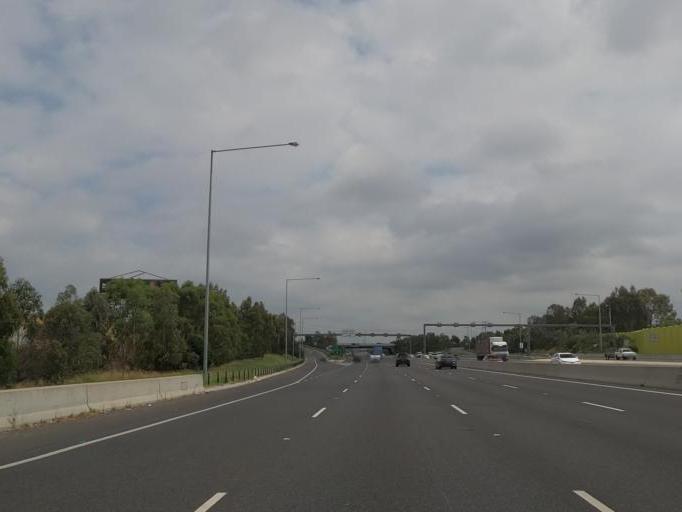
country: AU
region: Victoria
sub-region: Whittlesea
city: Thomastown
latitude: -37.6864
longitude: 145.0079
